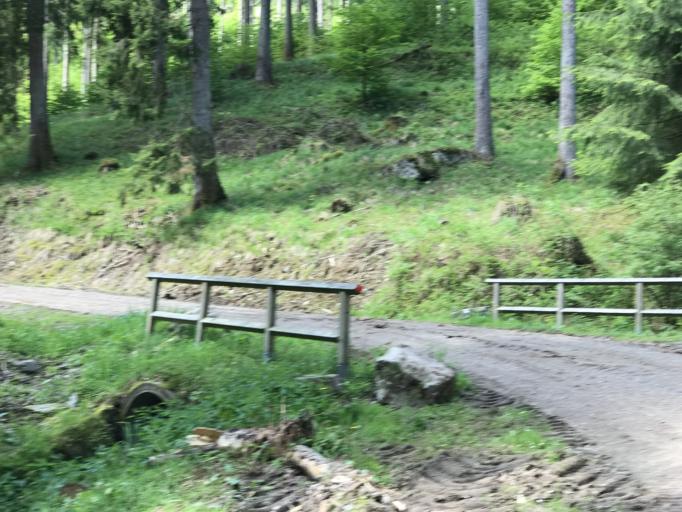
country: DE
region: Lower Saxony
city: Sankt Andreasberg
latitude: 51.7248
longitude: 10.4678
